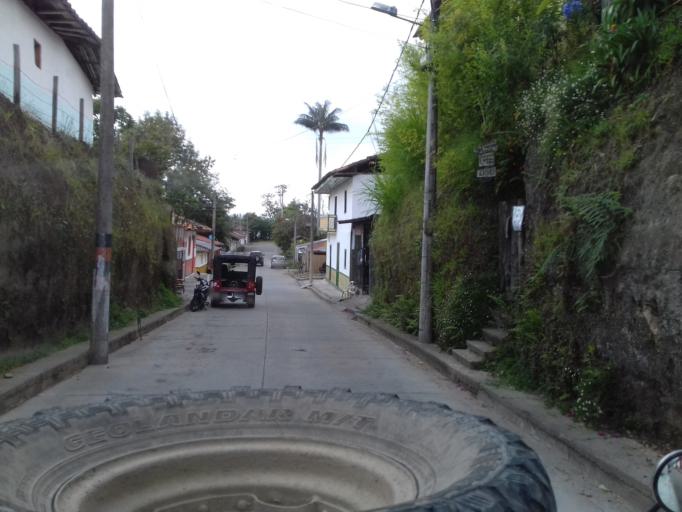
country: CO
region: Quindio
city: Salento
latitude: 4.6401
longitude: -75.5692
